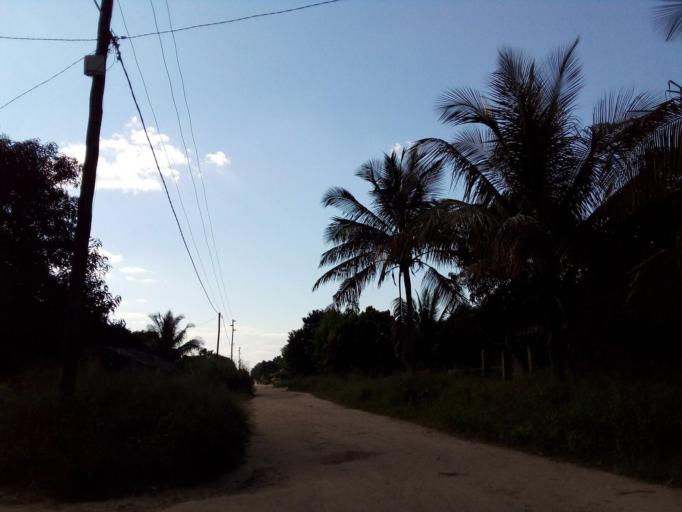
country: MZ
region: Zambezia
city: Quelimane
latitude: -17.5637
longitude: 36.6995
